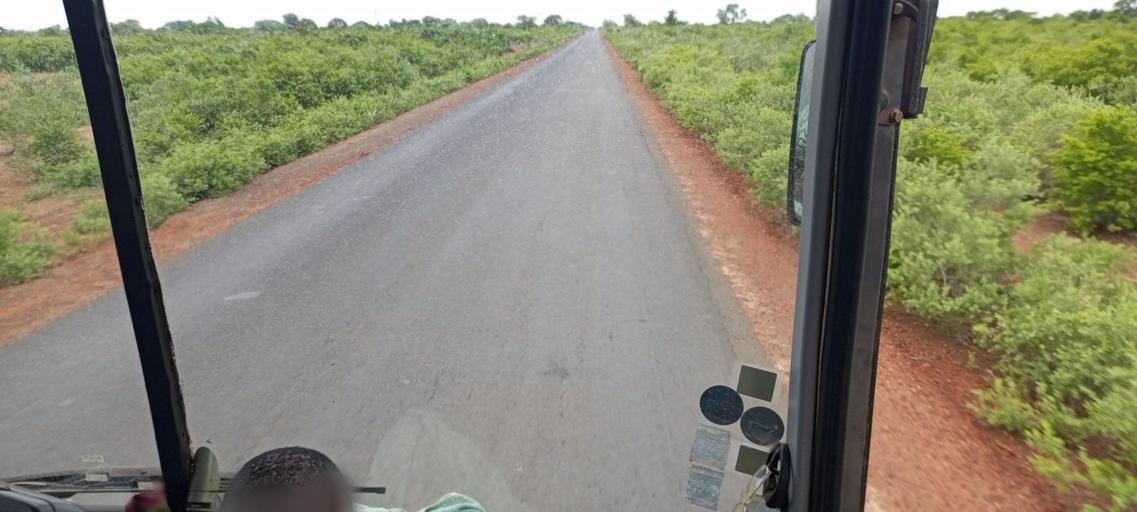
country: ML
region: Sikasso
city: Koutiala
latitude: 12.5638
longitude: -5.5959
